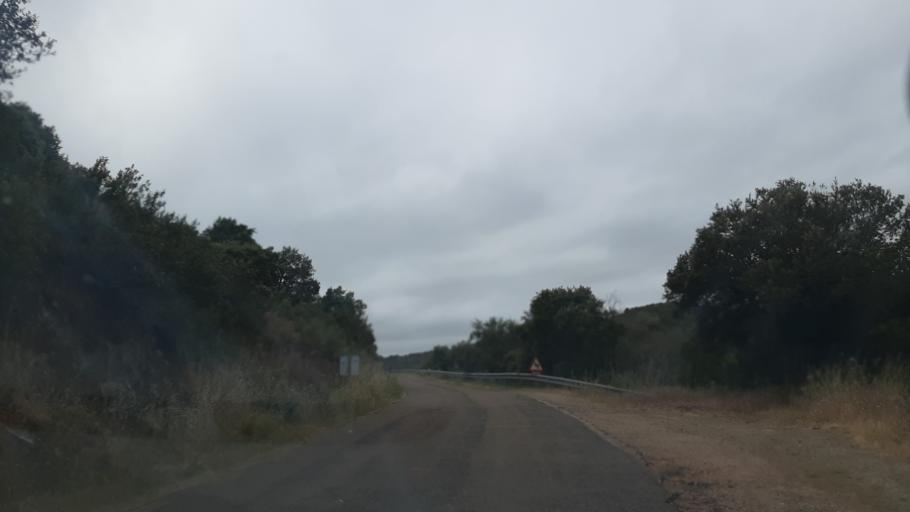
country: ES
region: Castille and Leon
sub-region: Provincia de Salamanca
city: Pastores
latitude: 40.5386
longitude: -6.4840
